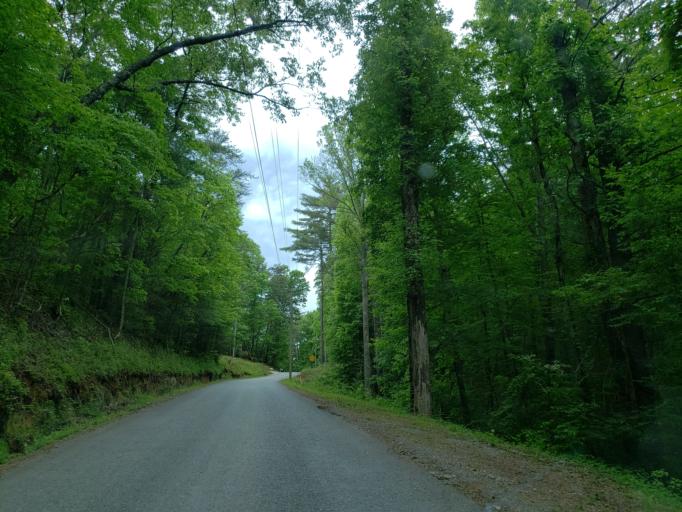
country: US
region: Georgia
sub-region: Fannin County
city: Blue Ridge
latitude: 34.8488
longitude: -84.4173
